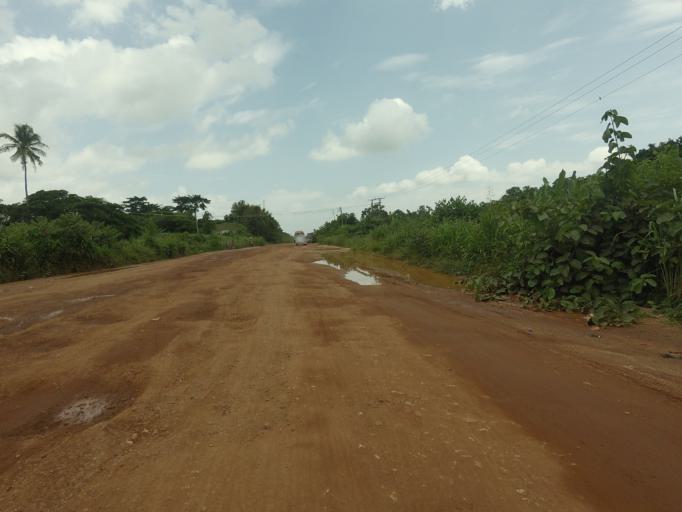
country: GH
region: Volta
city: Ho
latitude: 6.6813
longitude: 0.3297
